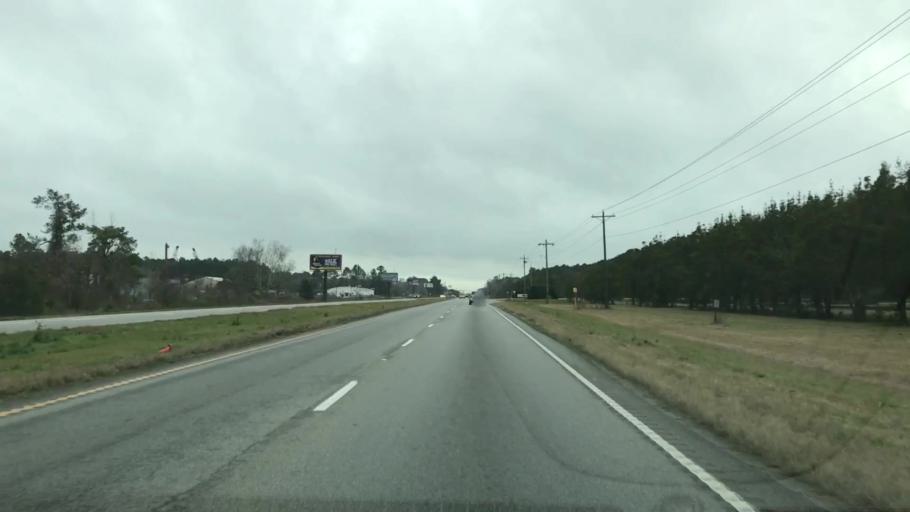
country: US
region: South Carolina
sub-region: Berkeley County
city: Goose Creek
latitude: 33.0408
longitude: -80.0335
